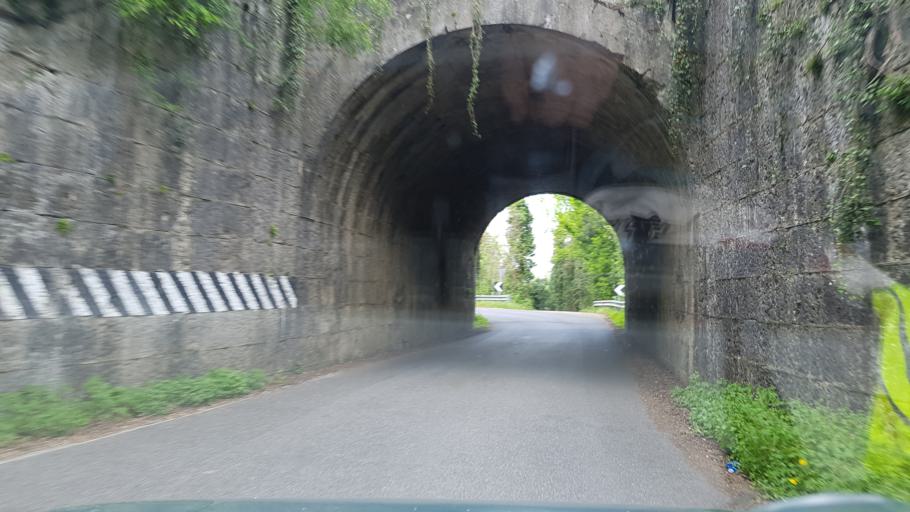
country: IT
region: Friuli Venezia Giulia
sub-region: Provincia di Gorizia
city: Savogna d'Isonzo
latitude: 45.8983
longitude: 13.5668
